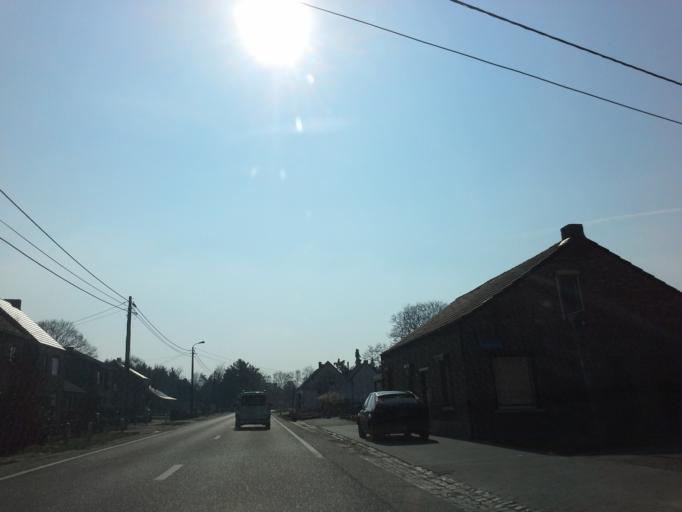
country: BE
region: Flanders
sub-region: Provincie Antwerpen
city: Meerhout
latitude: 51.1180
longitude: 5.0930
